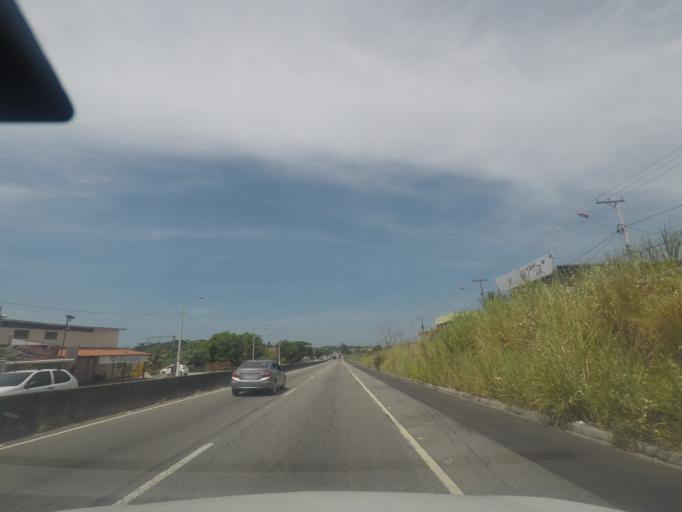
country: BR
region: Rio de Janeiro
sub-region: Marica
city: Marica
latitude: -22.9226
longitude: -42.8598
